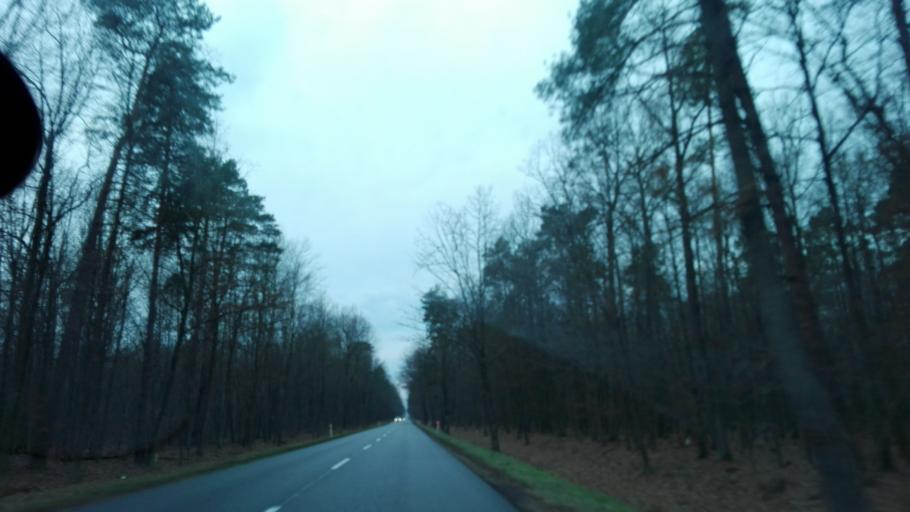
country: PL
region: Lublin Voivodeship
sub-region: Powiat radzynski
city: Wohyn
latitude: 51.7778
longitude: 22.8535
